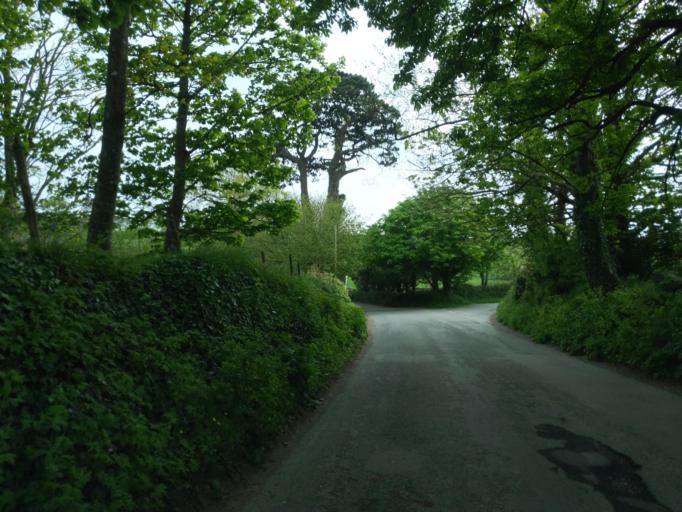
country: GB
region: England
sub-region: Devon
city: Dartmouth
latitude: 50.3586
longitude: -3.5470
